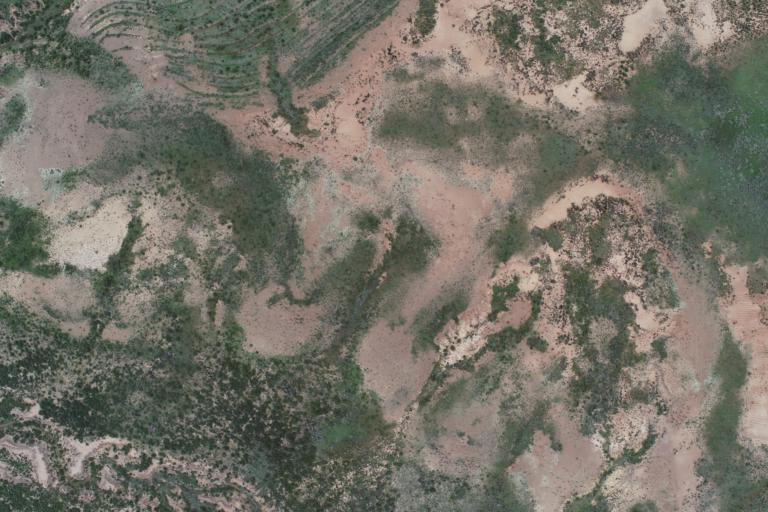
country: BO
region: La Paz
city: Curahuara de Carangas
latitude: -17.2943
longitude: -68.5093
